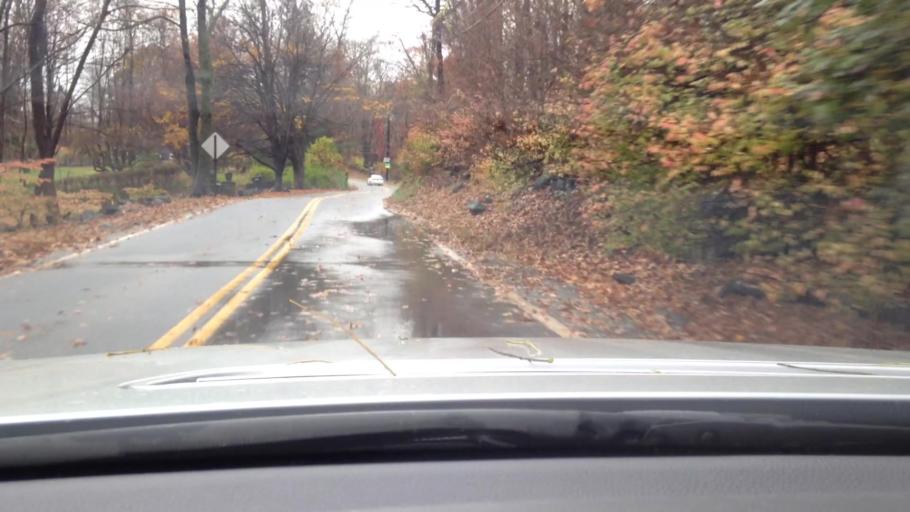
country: US
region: New York
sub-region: Westchester County
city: Croton-on-Hudson
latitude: 41.2201
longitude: -73.8779
